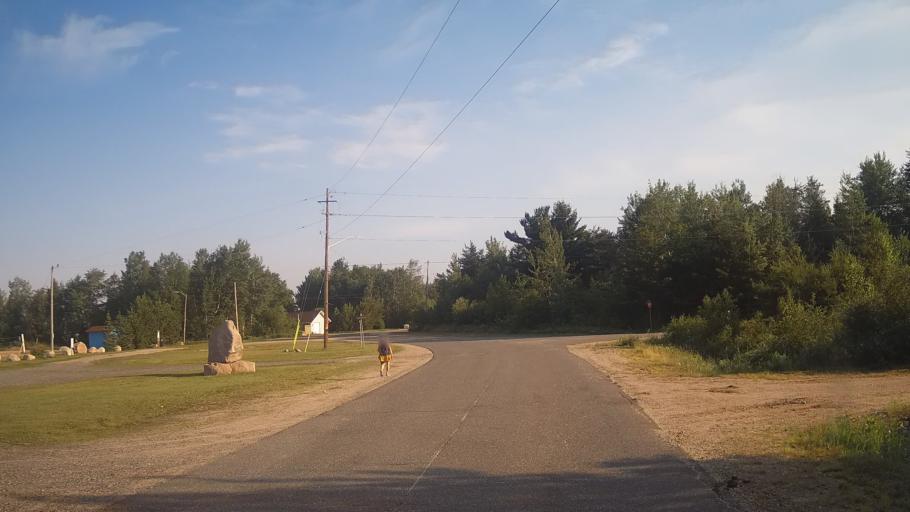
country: CA
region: Ontario
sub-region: Rainy River District
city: Atikokan
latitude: 49.4043
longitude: -91.6664
